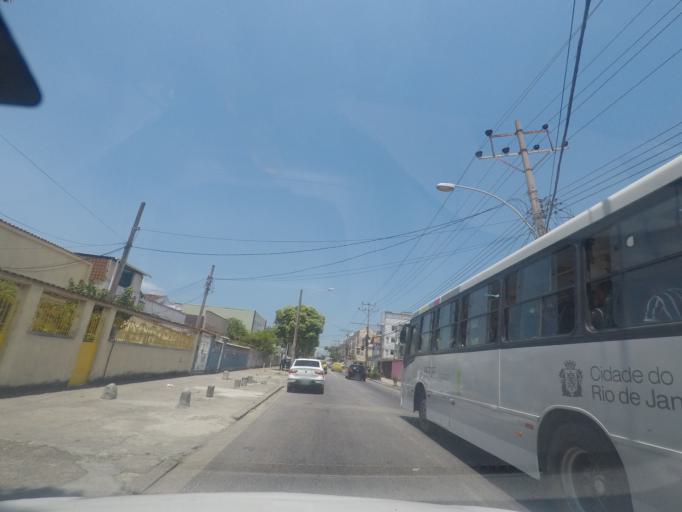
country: BR
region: Rio de Janeiro
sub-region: Duque De Caxias
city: Duque de Caxias
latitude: -22.8400
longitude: -43.2992
